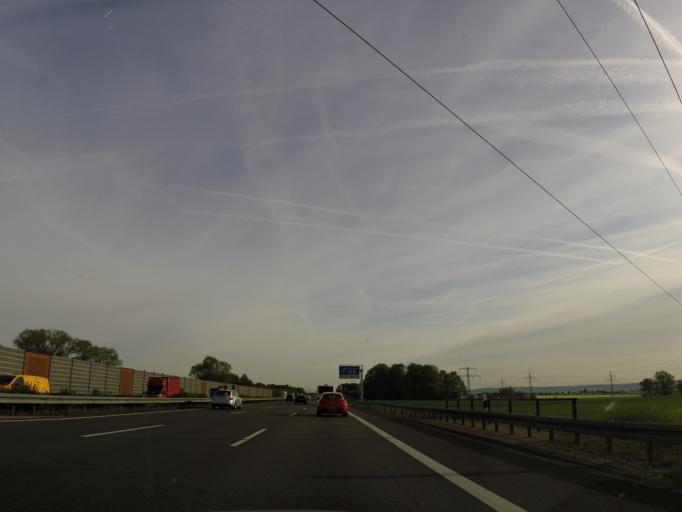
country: DE
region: Lower Saxony
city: Rosdorf
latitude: 51.4838
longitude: 9.8752
